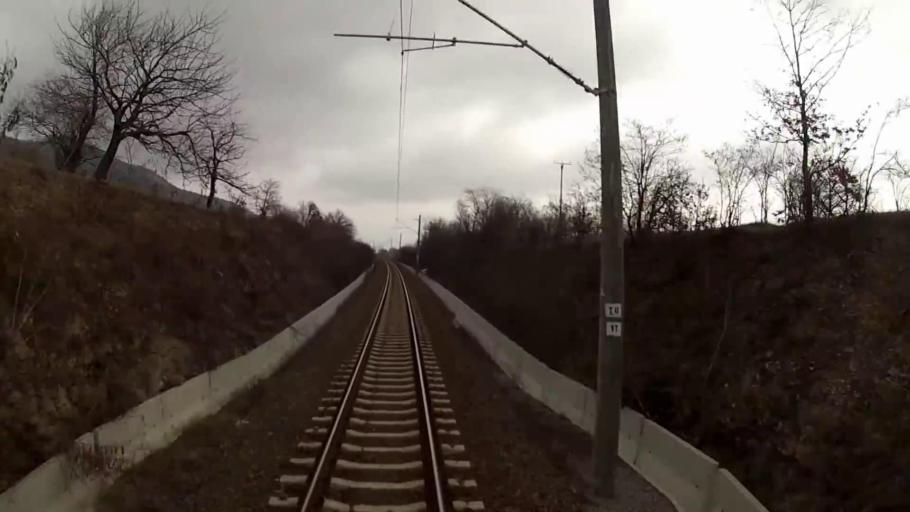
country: BG
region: Sofiya
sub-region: Obshtina Chavdar
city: Chavdar
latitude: 42.6919
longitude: 24.0371
